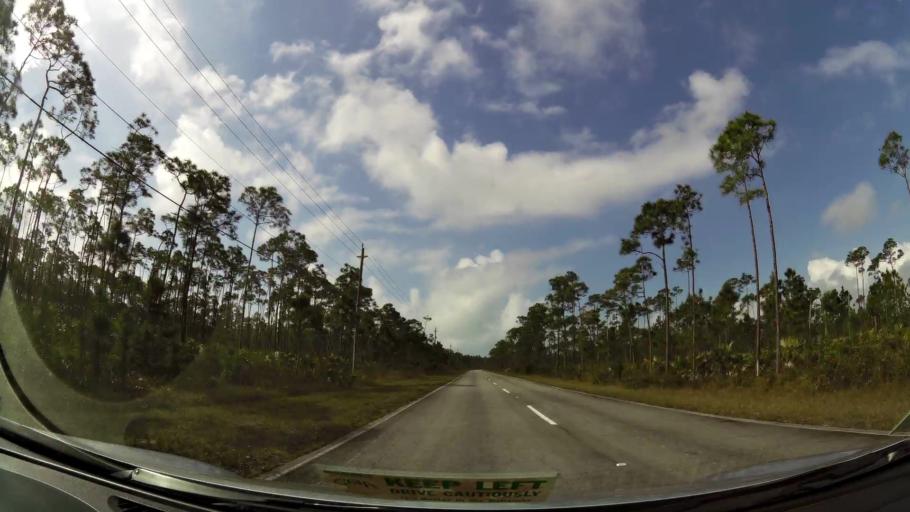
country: BS
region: Freeport
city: Lucaya
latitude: 26.5825
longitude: -78.5484
